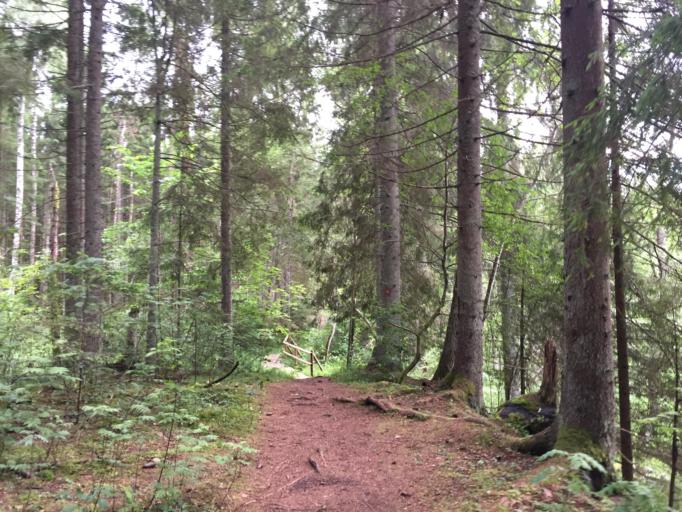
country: LV
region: Ligatne
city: Ligatne
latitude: 57.2345
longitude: 25.1548
